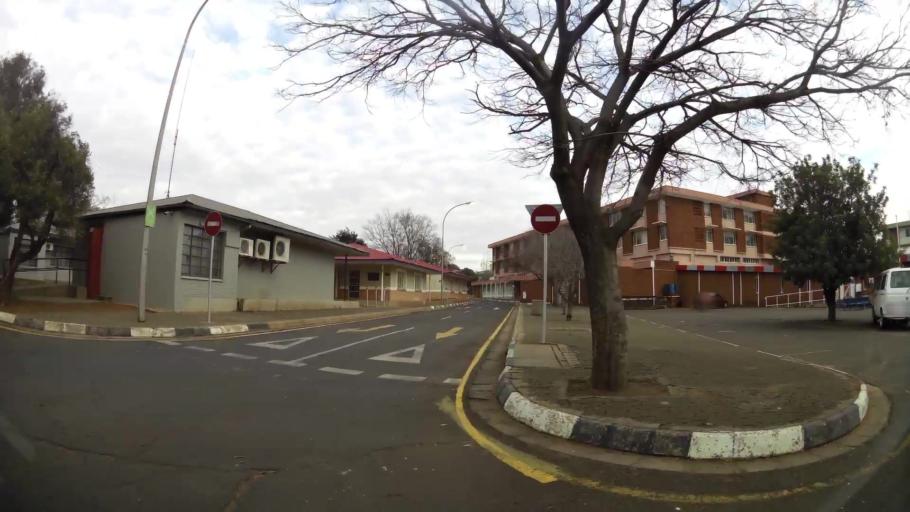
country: ZA
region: Orange Free State
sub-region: Mangaung Metropolitan Municipality
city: Bloemfontein
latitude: -29.1093
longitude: 26.1899
